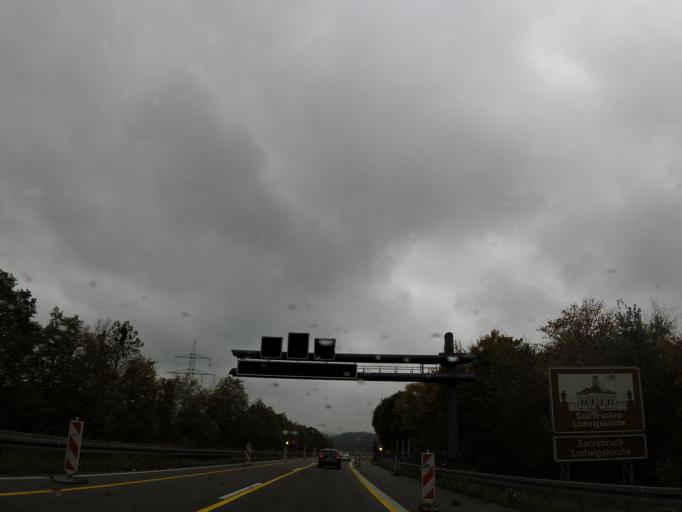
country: DE
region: Saarland
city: Sankt Ingbert
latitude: 49.2202
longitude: 7.0754
